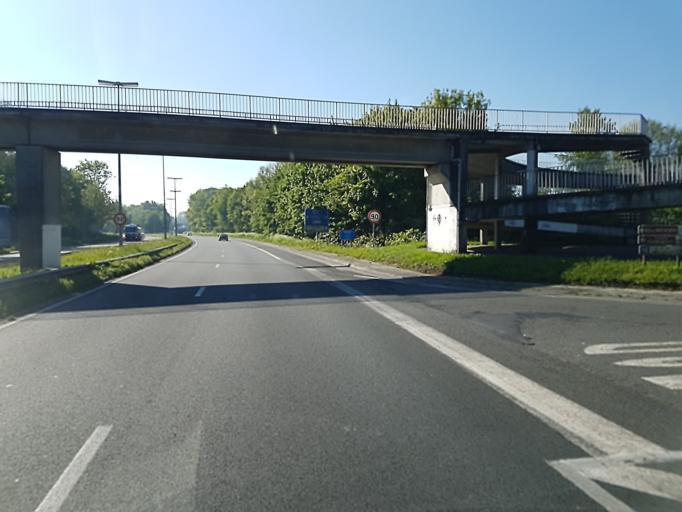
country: BE
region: Wallonia
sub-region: Province du Hainaut
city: Mouscron
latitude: 50.7538
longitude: 3.2059
